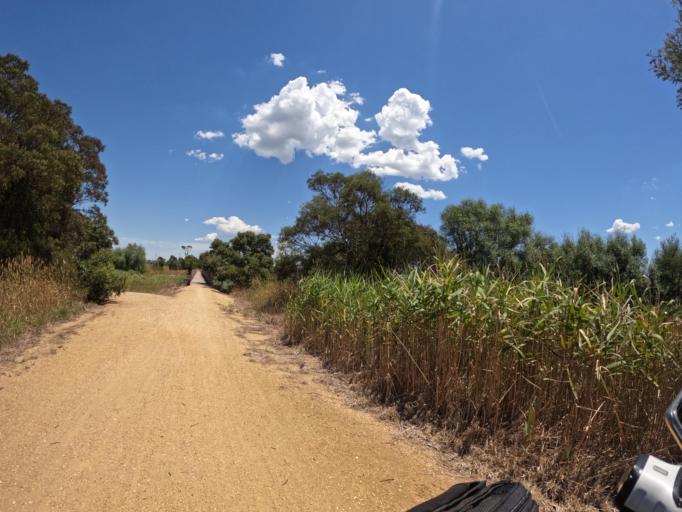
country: AU
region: Victoria
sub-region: Wellington
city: Heyfield
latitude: -37.9683
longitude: 146.8783
